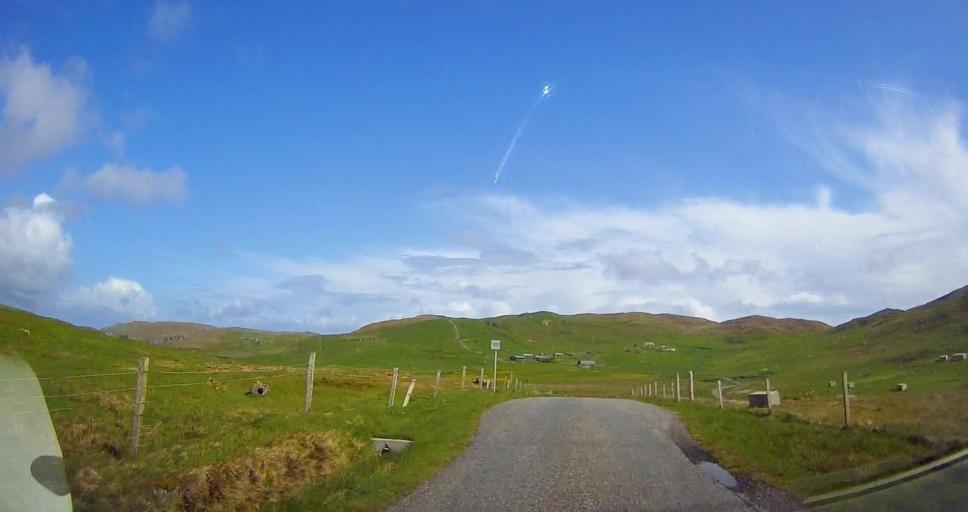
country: GB
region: Scotland
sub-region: Shetland Islands
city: Lerwick
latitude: 60.5941
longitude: -1.3277
